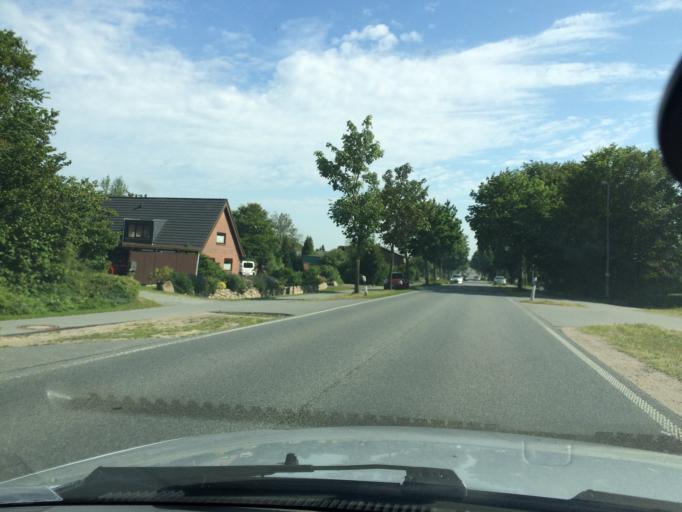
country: DE
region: Schleswig-Holstein
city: Jarplund-Weding
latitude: 54.7478
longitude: 9.4373
